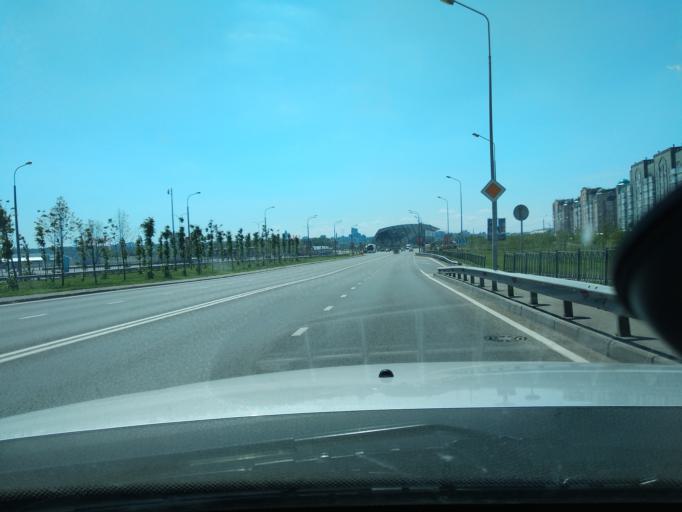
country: RU
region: Tatarstan
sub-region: Gorod Kazan'
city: Kazan
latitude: 55.8230
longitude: 49.1569
